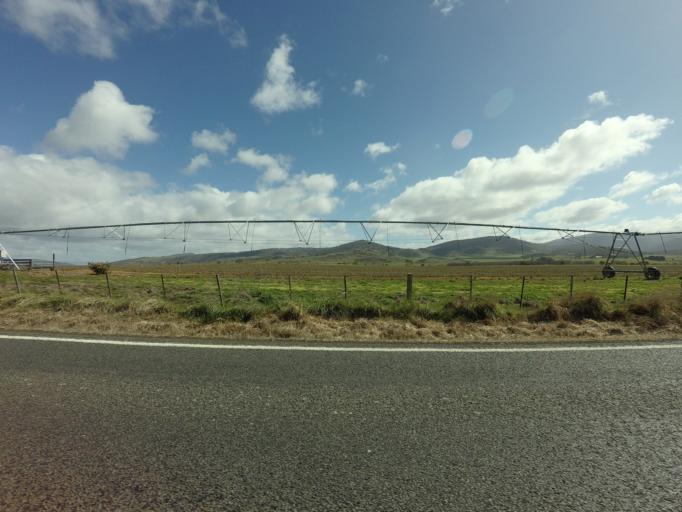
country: AU
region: Tasmania
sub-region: Northern Midlands
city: Evandale
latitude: -41.7905
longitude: 147.7121
